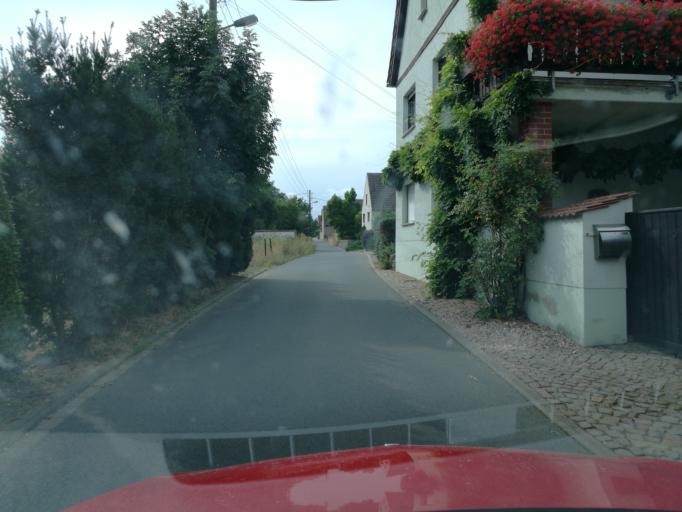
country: DE
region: Saxony
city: Oschatz
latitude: 51.2820
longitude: 13.0812
